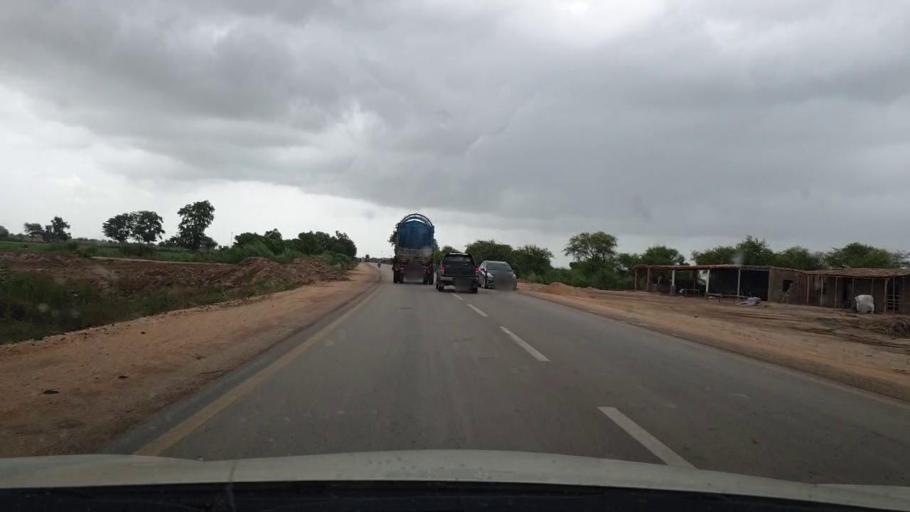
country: PK
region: Sindh
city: Kario
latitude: 24.6425
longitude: 68.4654
